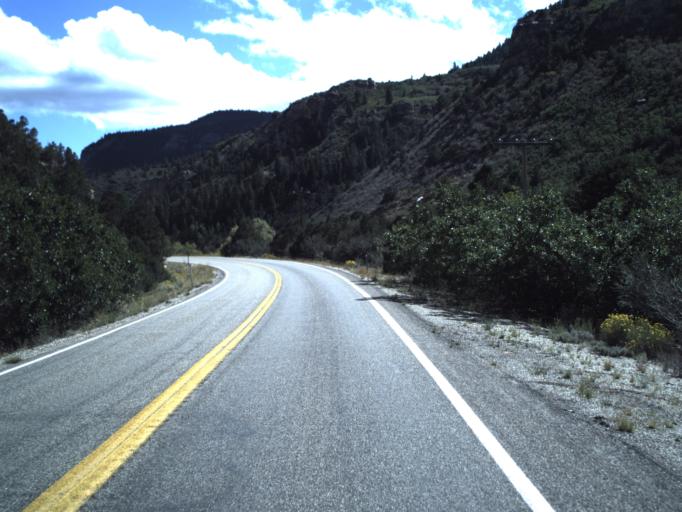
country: US
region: Utah
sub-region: Iron County
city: Cedar City
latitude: 37.6478
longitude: -112.9716
